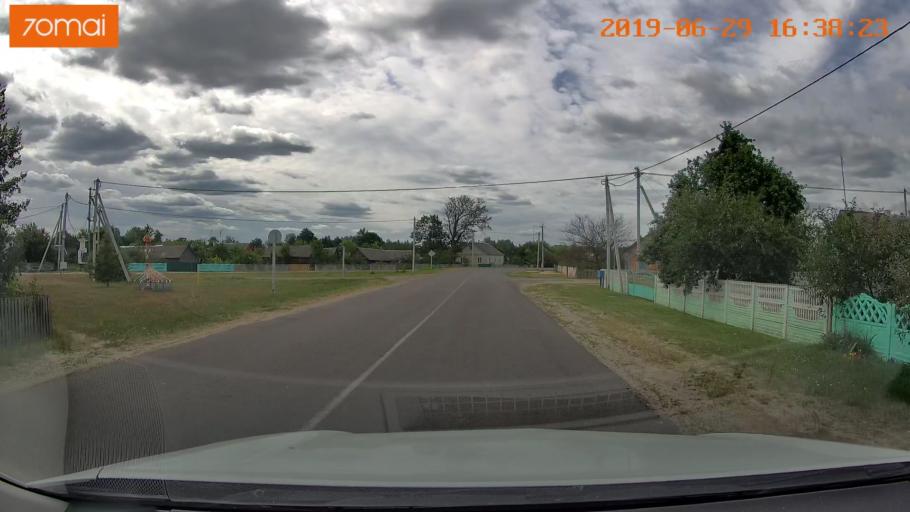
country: BY
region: Brest
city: Luninyets
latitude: 52.2323
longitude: 27.0162
